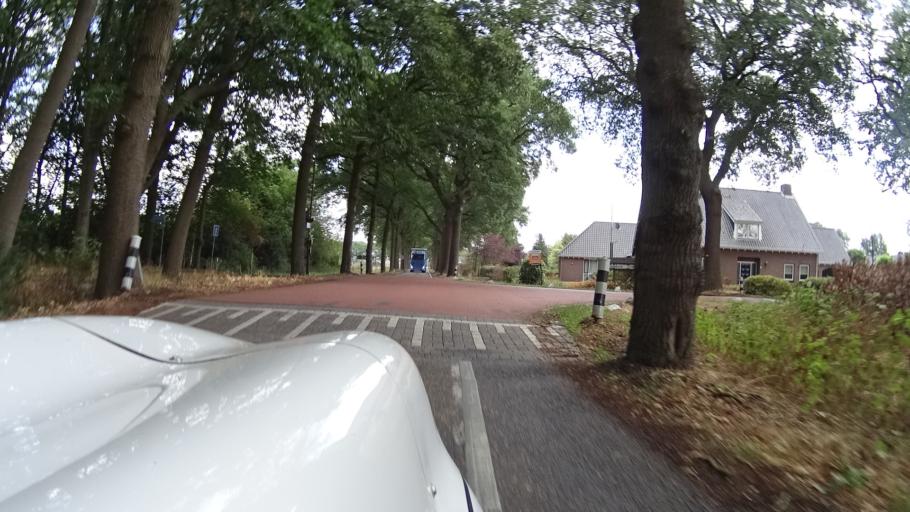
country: NL
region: North Brabant
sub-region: Gemeente Maasdonk
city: Geffen
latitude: 51.6951
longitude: 5.4472
